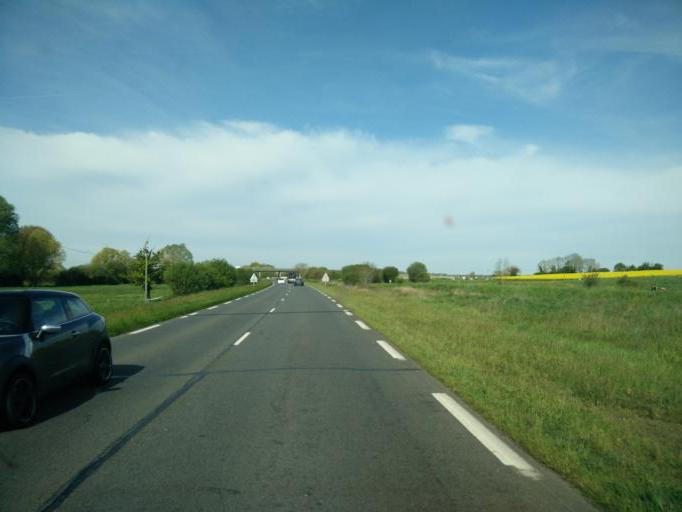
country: FR
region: Lower Normandy
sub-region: Departement de la Manche
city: Pontorson
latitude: 48.5623
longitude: -1.5055
